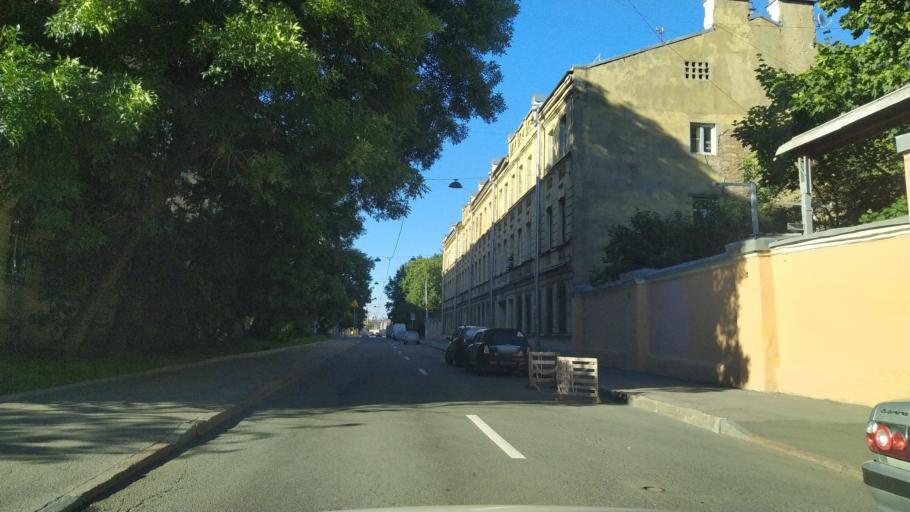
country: RU
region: St.-Petersburg
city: Centralniy
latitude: 59.9151
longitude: 30.3605
